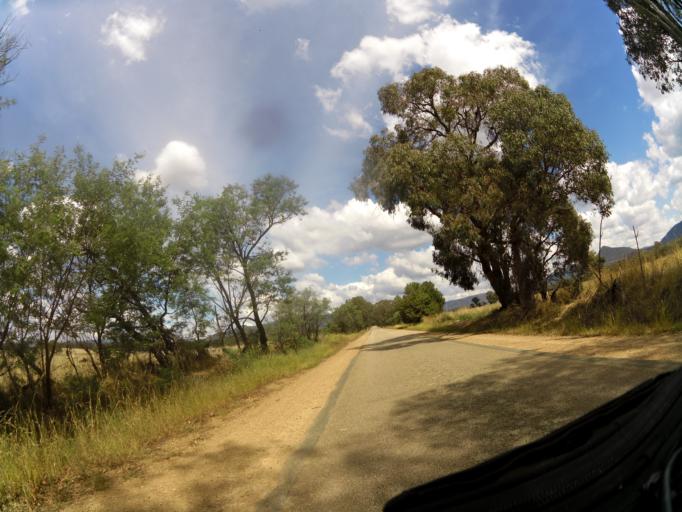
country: AU
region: Victoria
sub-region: Benalla
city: Benalla
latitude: -36.7573
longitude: 145.9780
